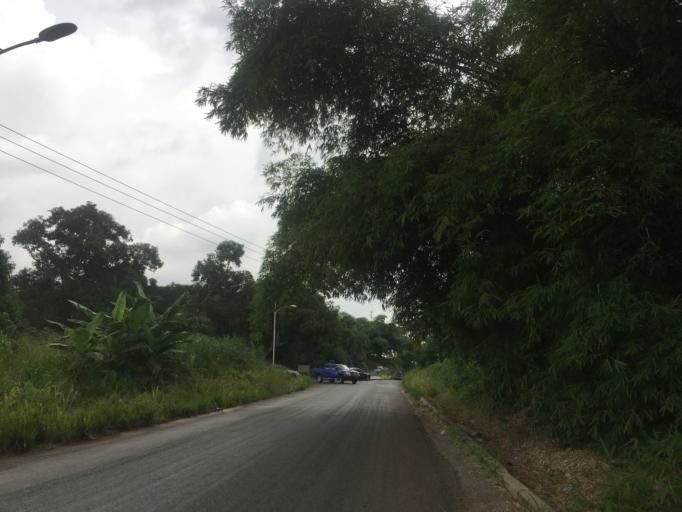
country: GH
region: Ashanti
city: Mamponteng
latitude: 6.6803
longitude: -1.5652
